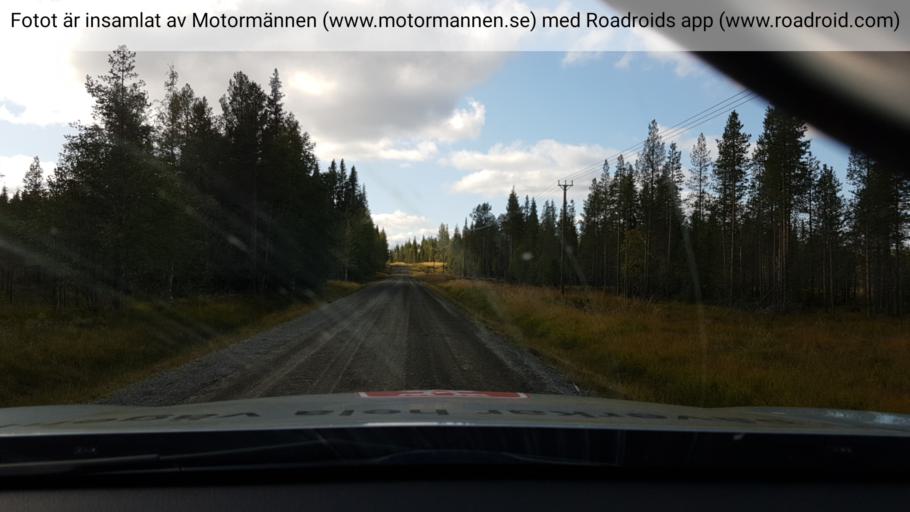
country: SE
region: Vaesterbotten
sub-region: Mala Kommun
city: Mala
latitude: 65.4922
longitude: 18.2628
